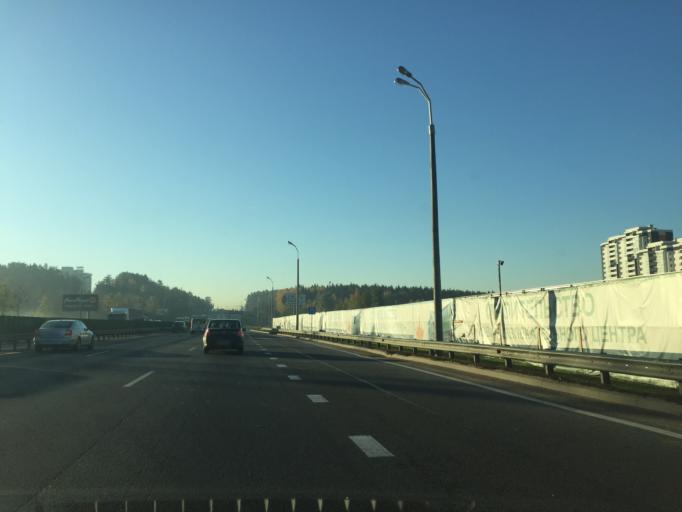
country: BY
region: Minsk
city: Borovlyany
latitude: 53.9330
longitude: 27.6761
